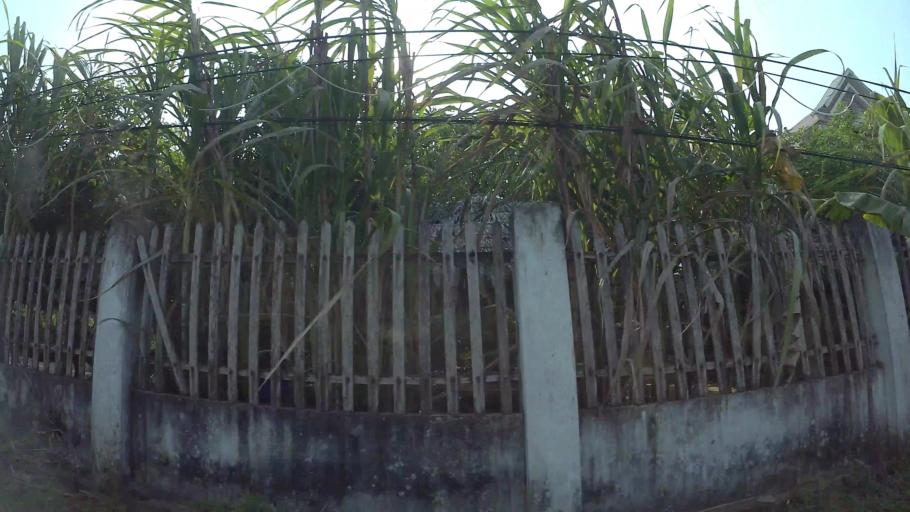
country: VN
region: Da Nang
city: Cam Le
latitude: 16.0138
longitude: 108.1852
